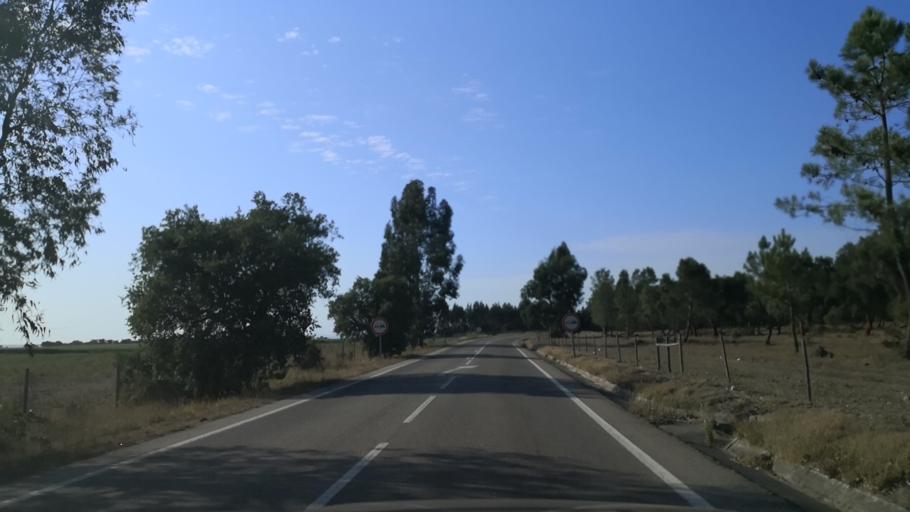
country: PT
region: Santarem
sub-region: Almeirim
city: Fazendas de Almeirim
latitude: 39.1267
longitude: -8.6043
